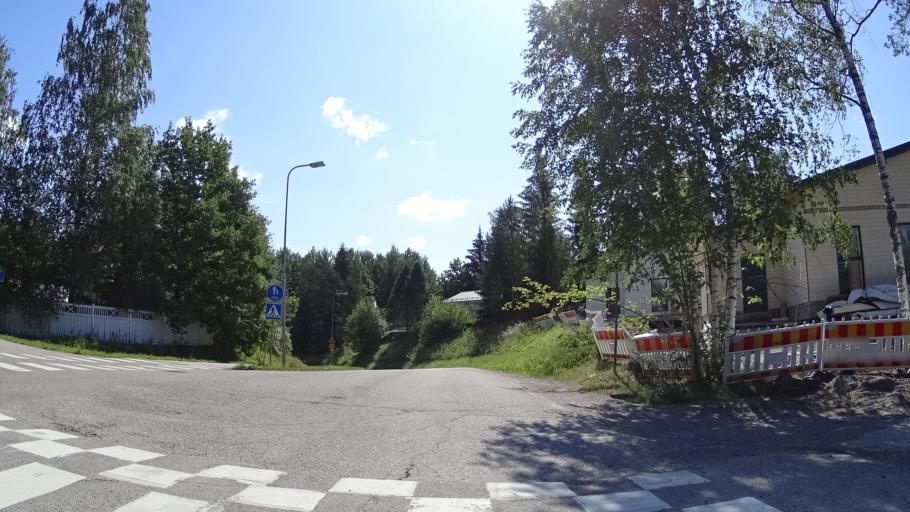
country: FI
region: Uusimaa
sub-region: Helsinki
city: Jaervenpaeae
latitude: 60.4466
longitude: 25.1017
